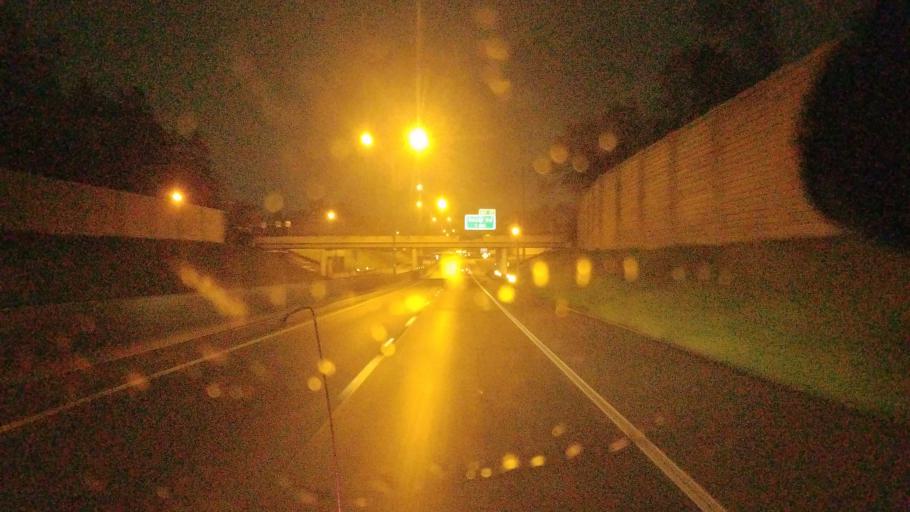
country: US
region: Ohio
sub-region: Lucas County
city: Ottawa Hills
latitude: 41.6879
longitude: -83.6459
